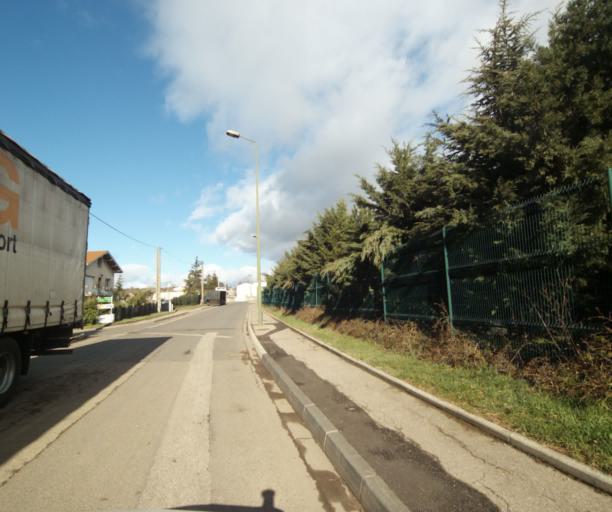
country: FR
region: Rhone-Alpes
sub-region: Departement de la Loire
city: La Talaudiere
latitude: 45.4634
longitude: 4.4233
